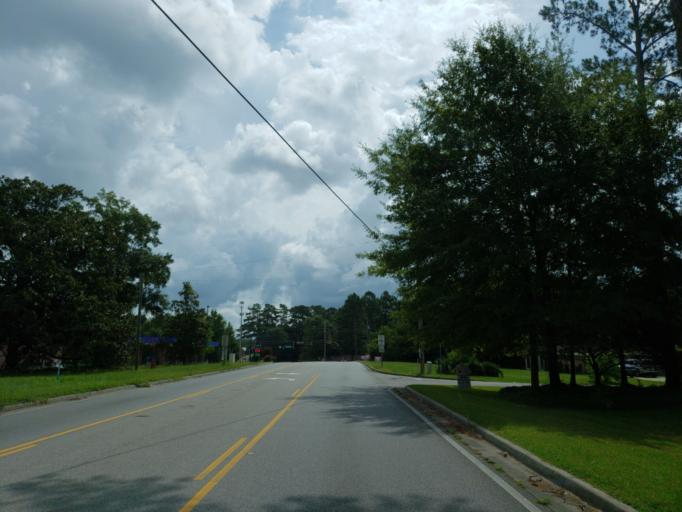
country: US
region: Mississippi
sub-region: Lamar County
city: Arnold Line
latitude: 31.3369
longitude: -89.3590
